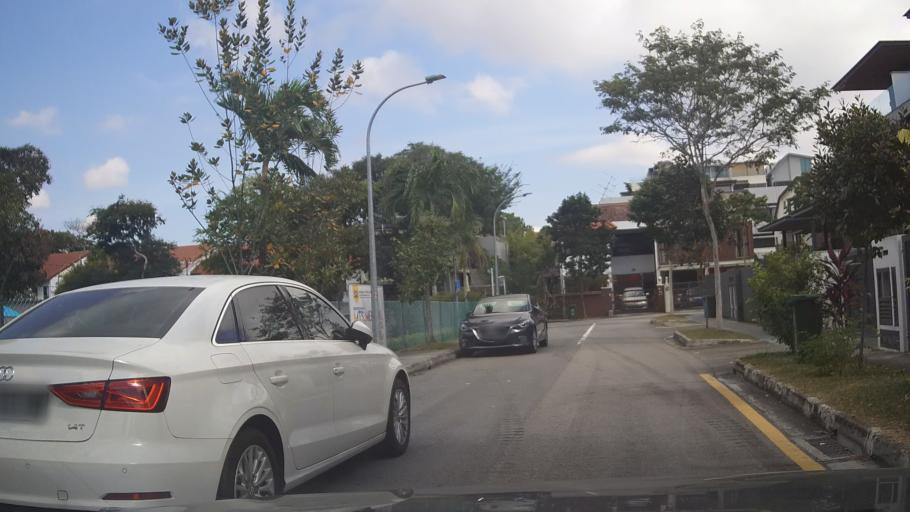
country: SG
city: Singapore
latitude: 1.3115
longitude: 103.9291
